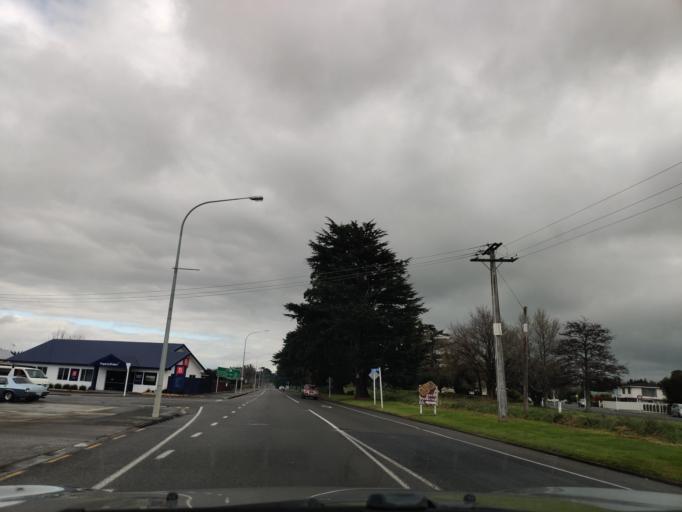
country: NZ
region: Manawatu-Wanganui
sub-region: Palmerston North City
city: Palmerston North
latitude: -40.2106
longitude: 176.0937
